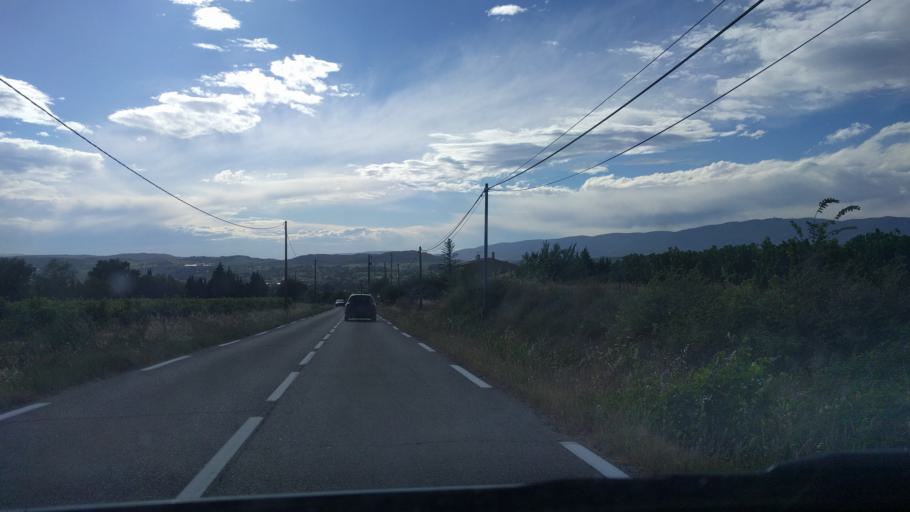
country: FR
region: Provence-Alpes-Cote d'Azur
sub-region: Departement du Vaucluse
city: Grambois
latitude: 43.7292
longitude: 5.5740
